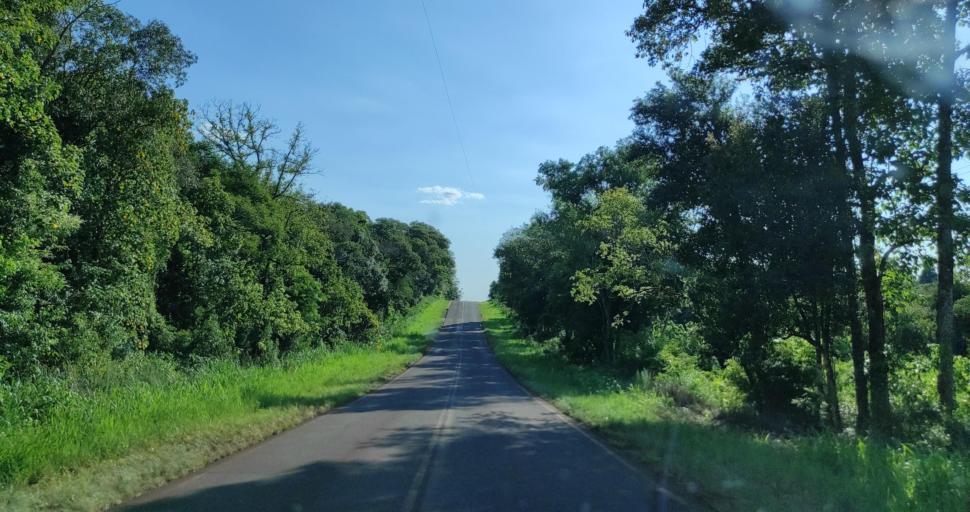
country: AR
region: Misiones
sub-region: Departamento de Eldorado
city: Eldorado
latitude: -26.3914
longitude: -54.3594
